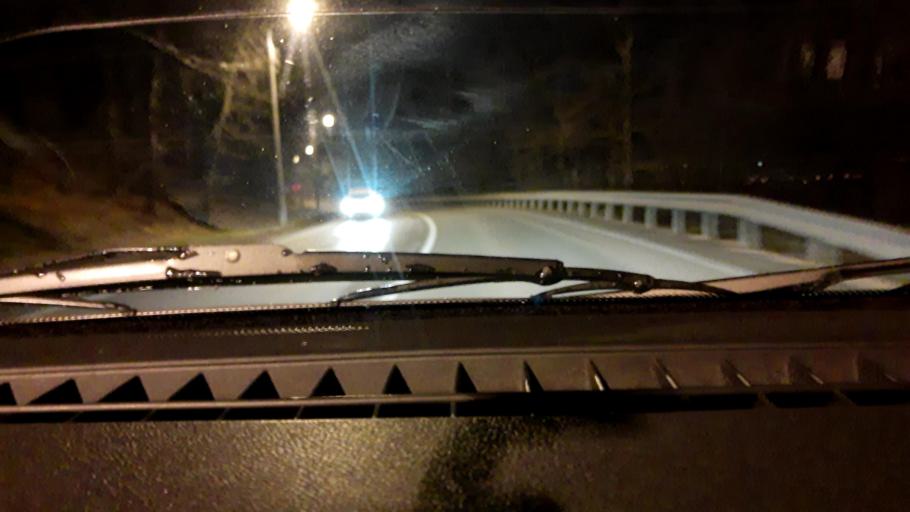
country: RU
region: Bashkortostan
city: Ufa
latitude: 54.8560
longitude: 56.0737
